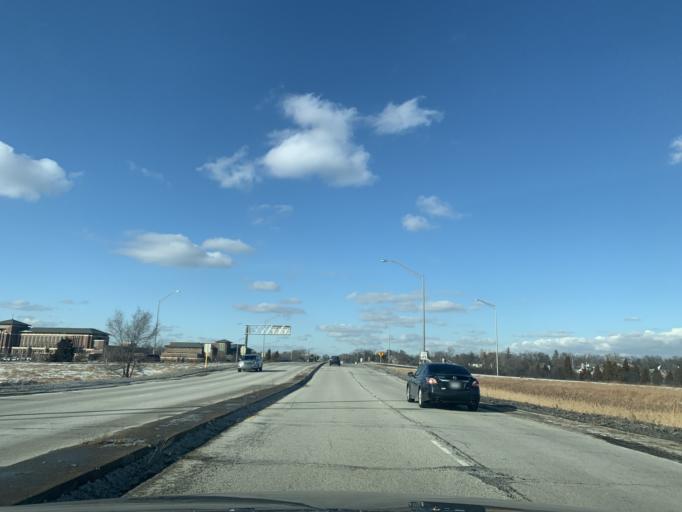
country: US
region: Illinois
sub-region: DuPage County
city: Oak Brook
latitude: 41.8597
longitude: -87.9302
